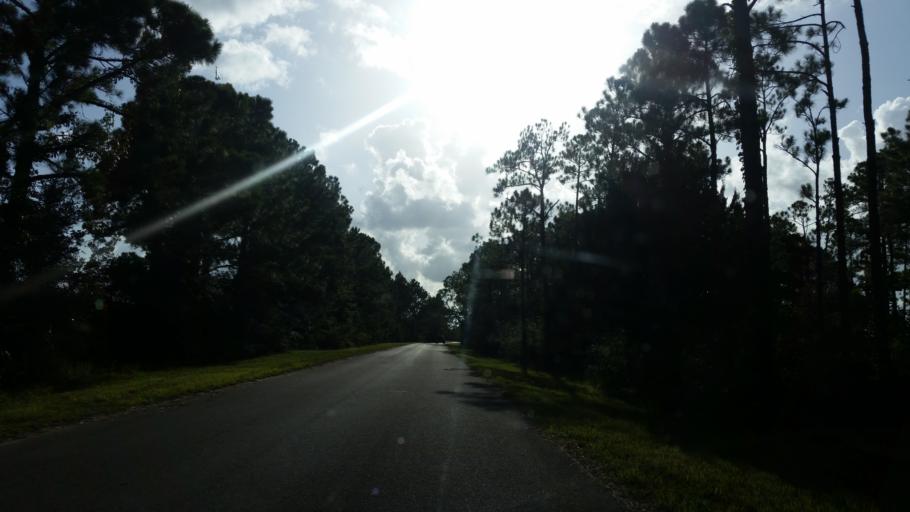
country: US
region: Florida
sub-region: Santa Rosa County
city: Pace
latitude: 30.5347
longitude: -87.1178
